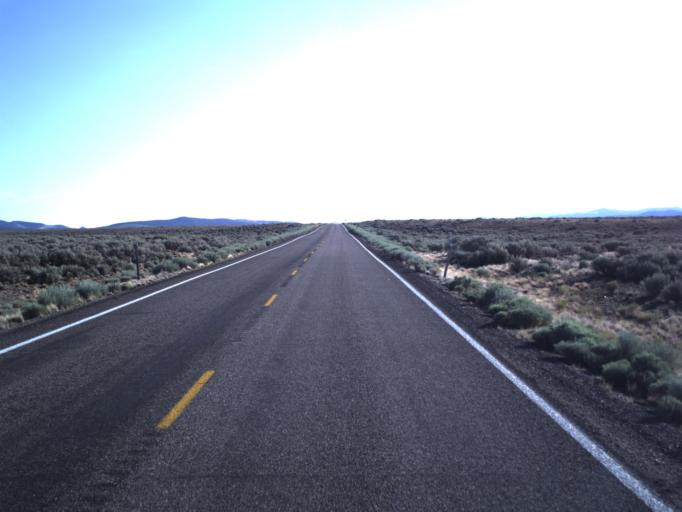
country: US
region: Utah
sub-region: Iron County
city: Enoch
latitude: 37.9364
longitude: -113.0250
